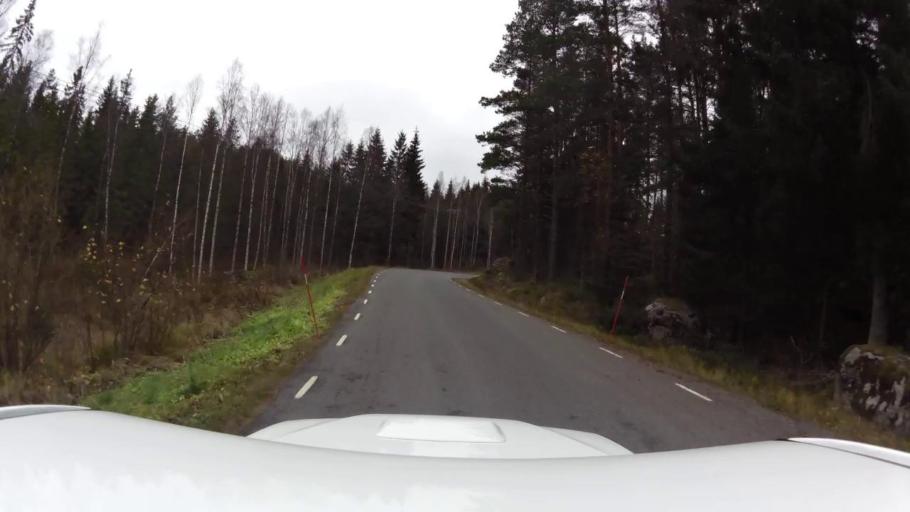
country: SE
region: OEstergoetland
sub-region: Kinda Kommun
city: Rimforsa
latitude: 58.1363
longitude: 15.5885
